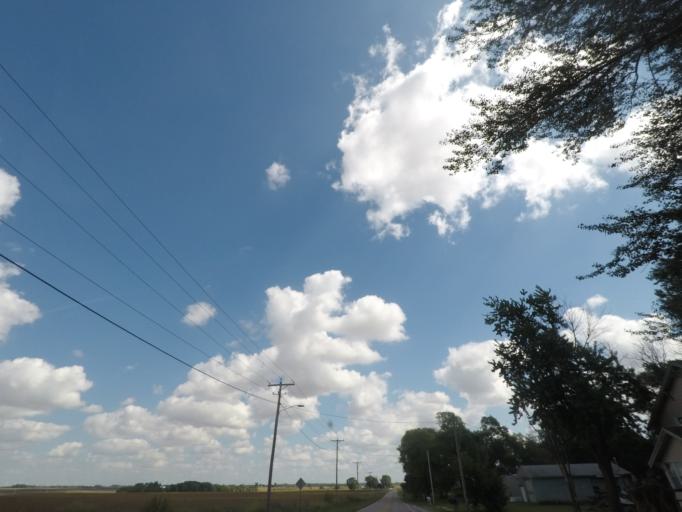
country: US
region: Iowa
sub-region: Story County
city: Nevada
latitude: 42.0706
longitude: -93.3941
